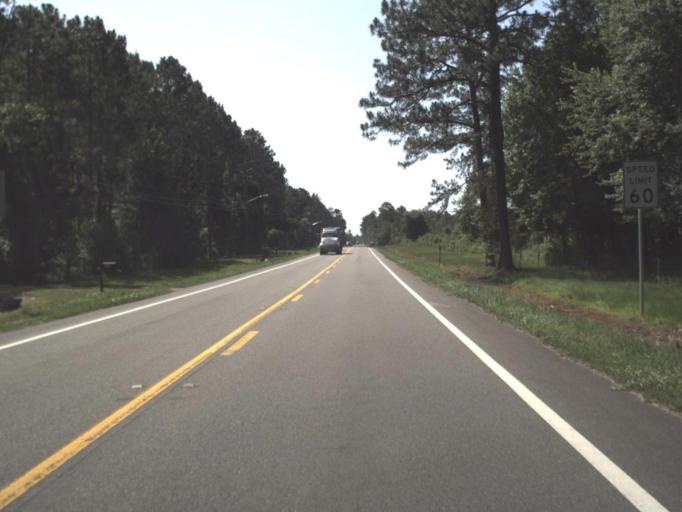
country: US
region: Florida
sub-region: Nassau County
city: Nassau Village-Ratliff
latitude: 30.5055
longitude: -81.7519
